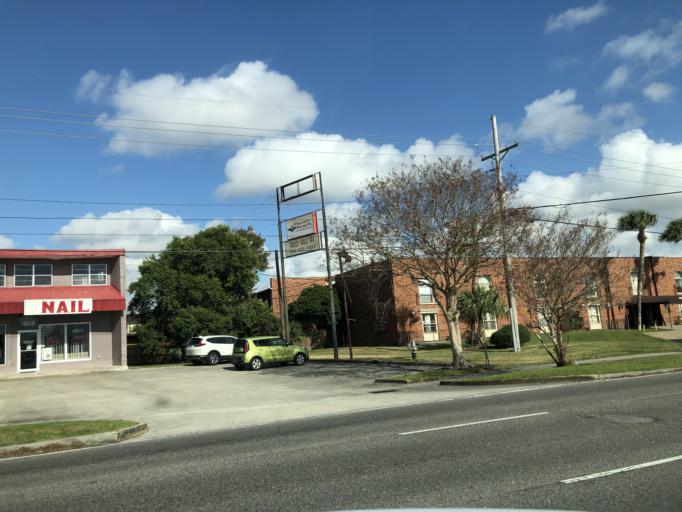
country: US
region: Louisiana
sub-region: Jefferson Parish
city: Kenner
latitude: 30.0052
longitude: -90.2179
